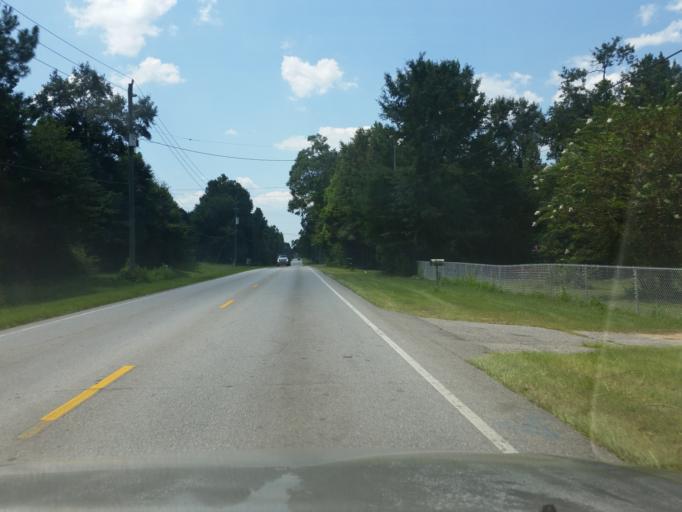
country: US
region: Florida
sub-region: Escambia County
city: Cantonment
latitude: 30.6387
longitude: -87.3187
